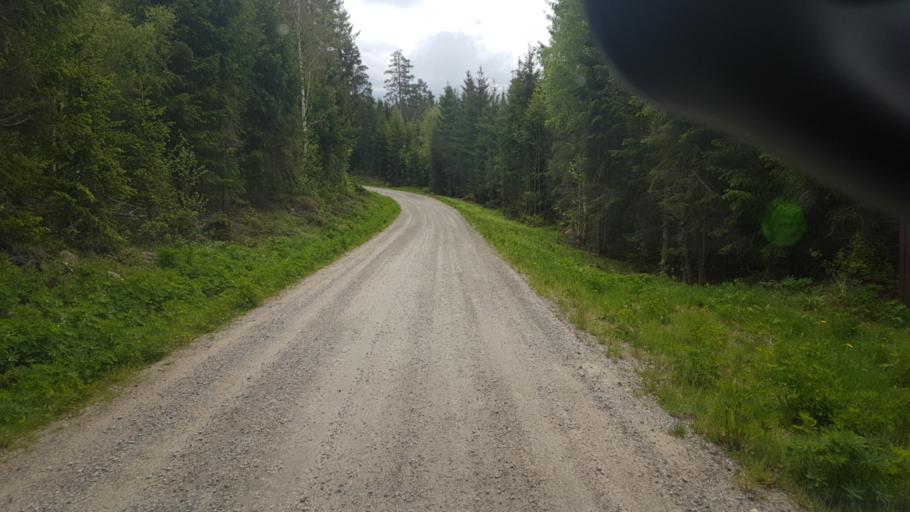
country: SE
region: Vaermland
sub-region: Arvika Kommun
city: Arvika
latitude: 59.8365
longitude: 12.7653
